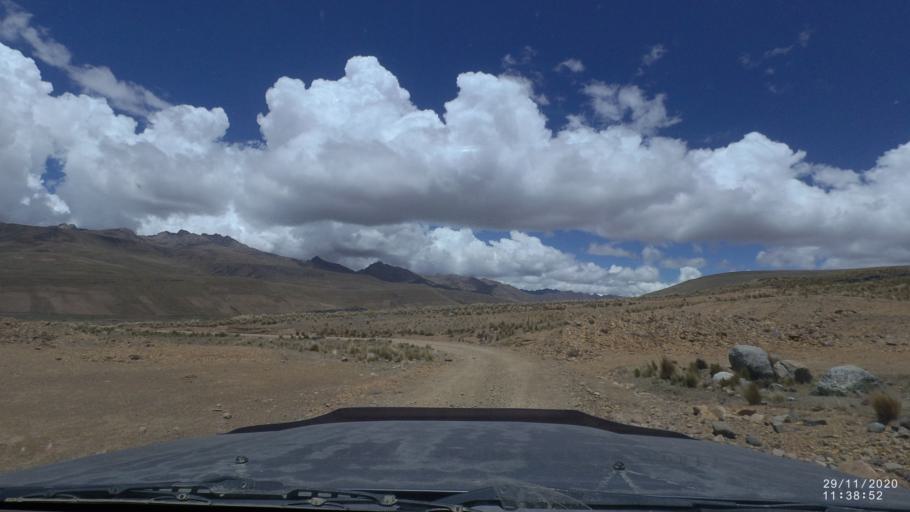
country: BO
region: Cochabamba
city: Cochabamba
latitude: -17.1972
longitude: -66.2369
